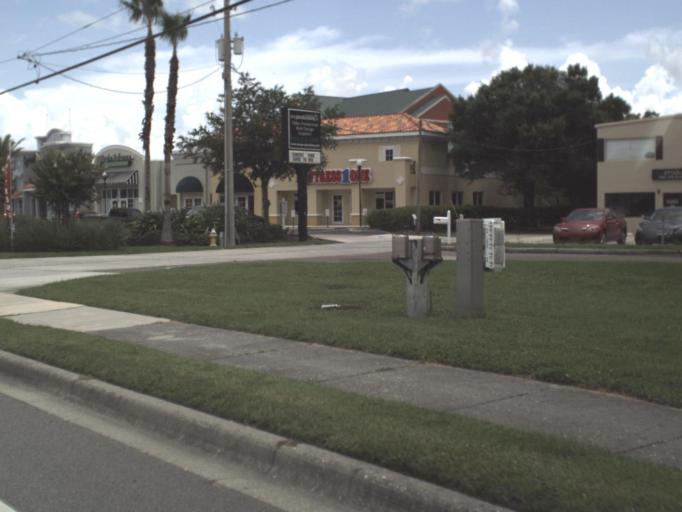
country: US
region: Florida
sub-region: Pinellas County
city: Oldsmar
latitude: 28.0360
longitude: -82.6559
